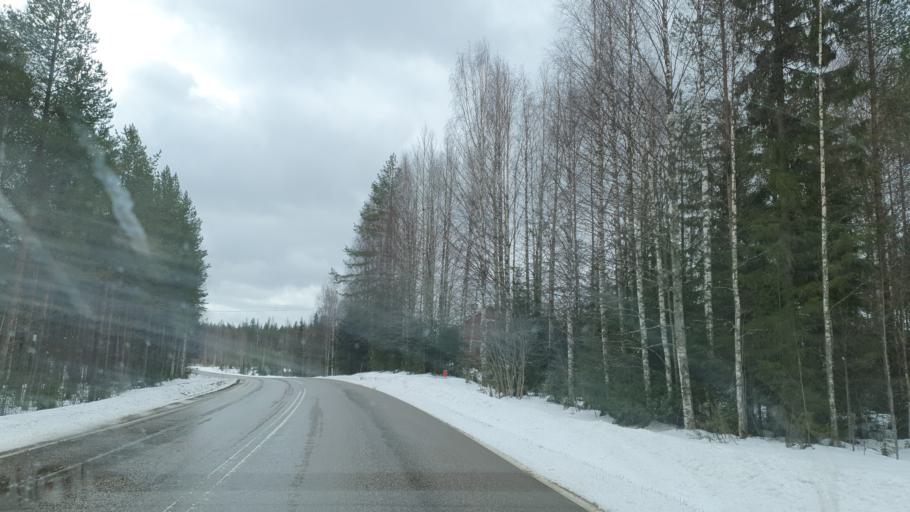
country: FI
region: Kainuu
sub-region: Kehys-Kainuu
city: Puolanka
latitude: 65.1401
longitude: 27.6821
